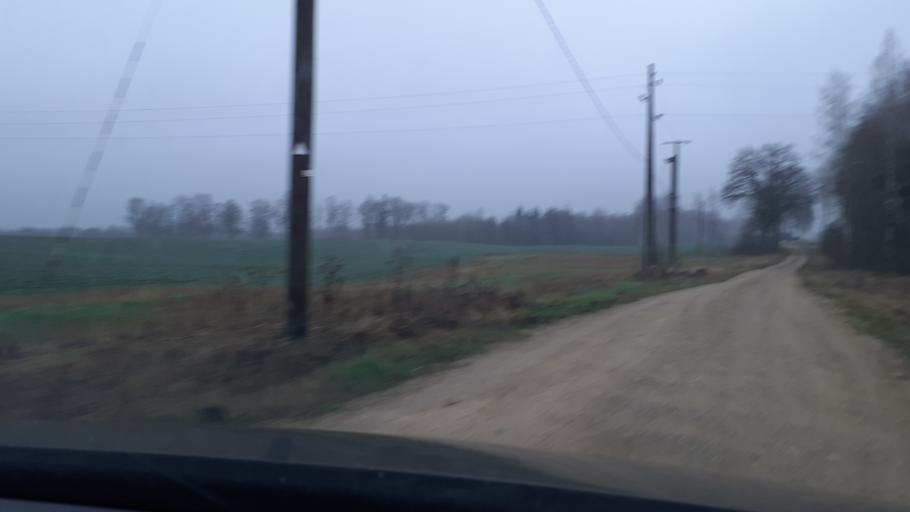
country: LV
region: Alsunga
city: Alsunga
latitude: 56.8908
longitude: 21.6704
